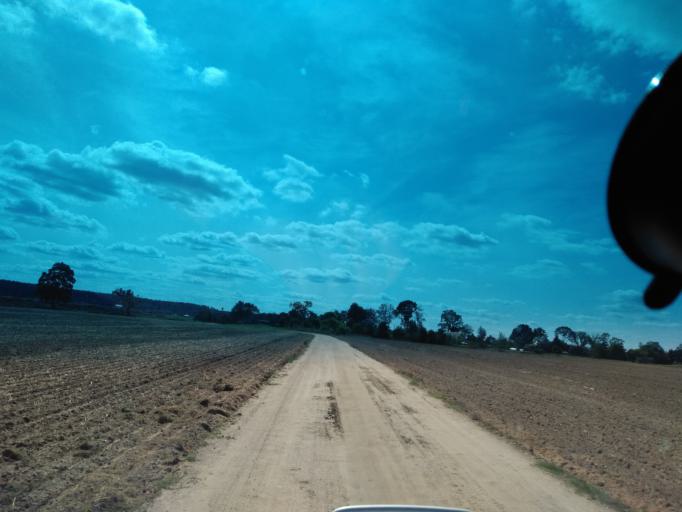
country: BY
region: Minsk
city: Stan'kava
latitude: 53.6373
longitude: 27.3081
